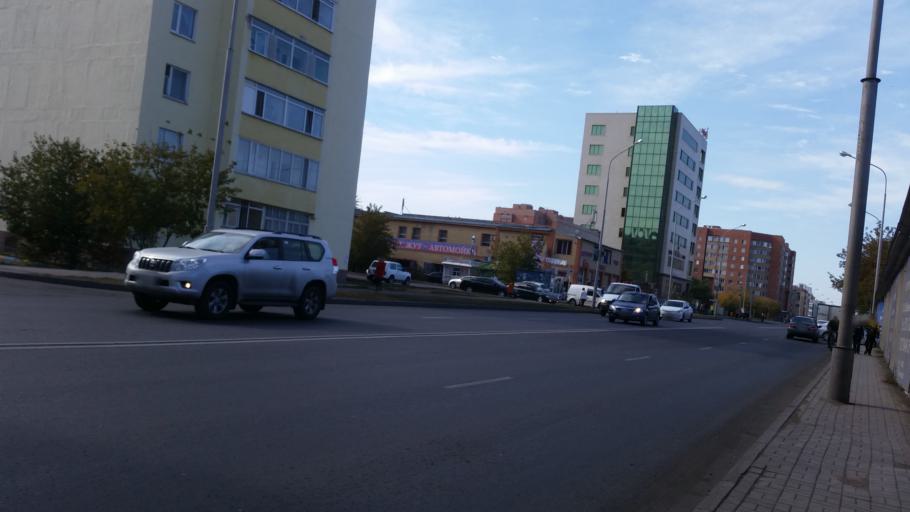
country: KZ
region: Astana Qalasy
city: Astana
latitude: 51.1587
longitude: 71.4933
